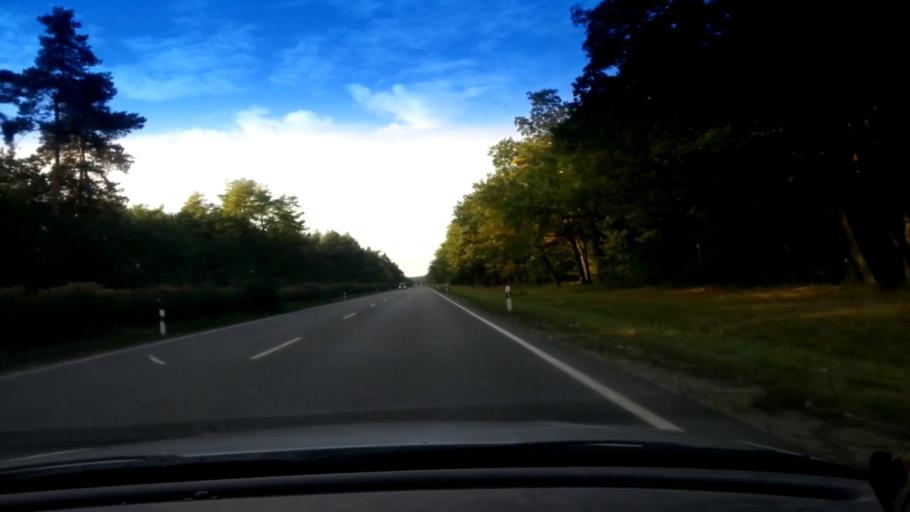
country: DE
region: Bavaria
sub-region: Upper Franconia
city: Strullendorf
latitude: 49.8511
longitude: 10.9598
